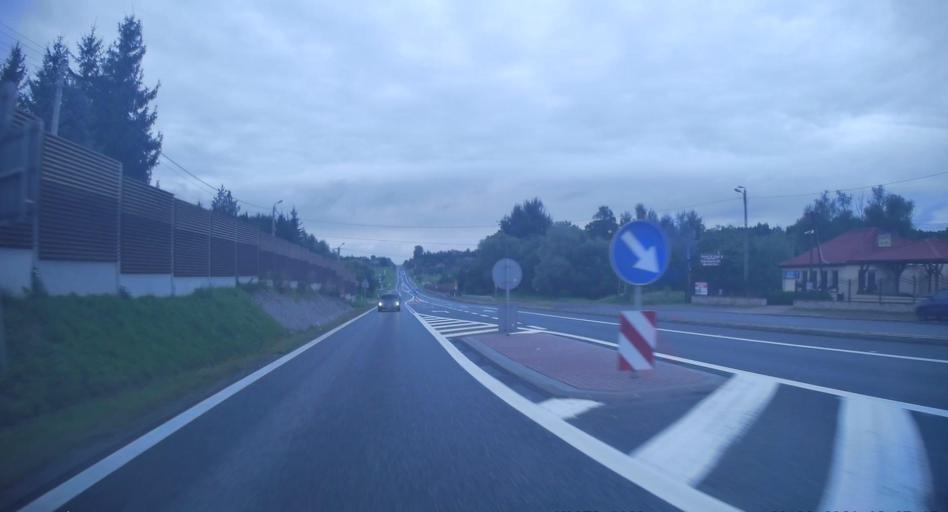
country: PL
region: Lesser Poland Voivodeship
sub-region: Powiat wielicki
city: Tomaszkowice
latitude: 49.9842
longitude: 20.1126
